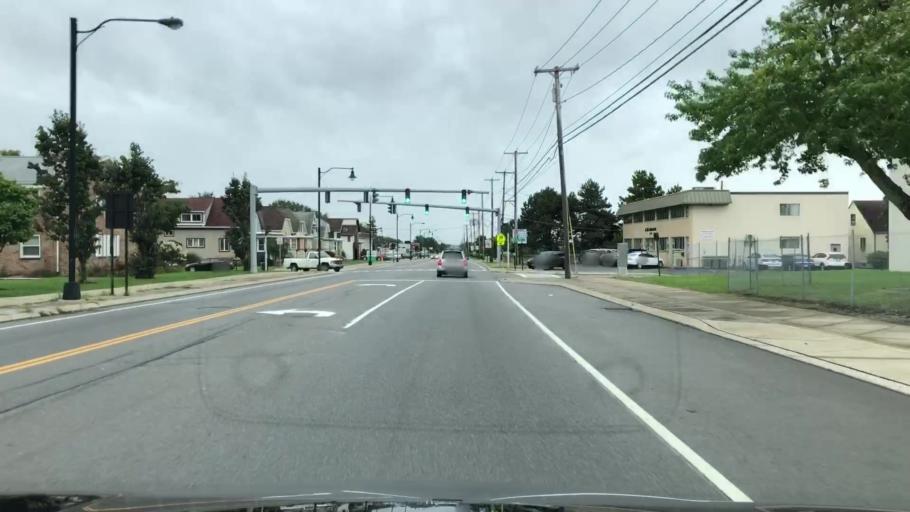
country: US
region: New York
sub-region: Erie County
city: Eggertsville
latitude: 42.9420
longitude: -78.7842
